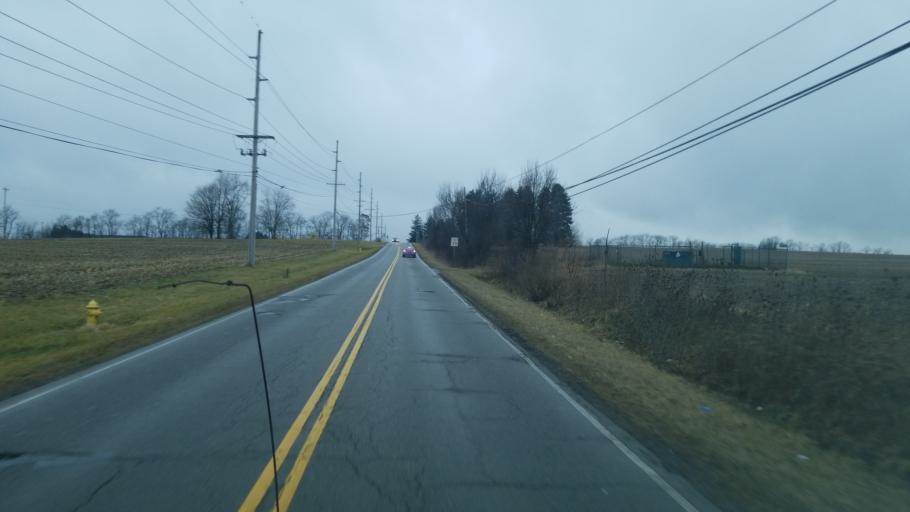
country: US
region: Ohio
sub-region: Wayne County
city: Wooster
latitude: 40.8285
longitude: -81.8986
